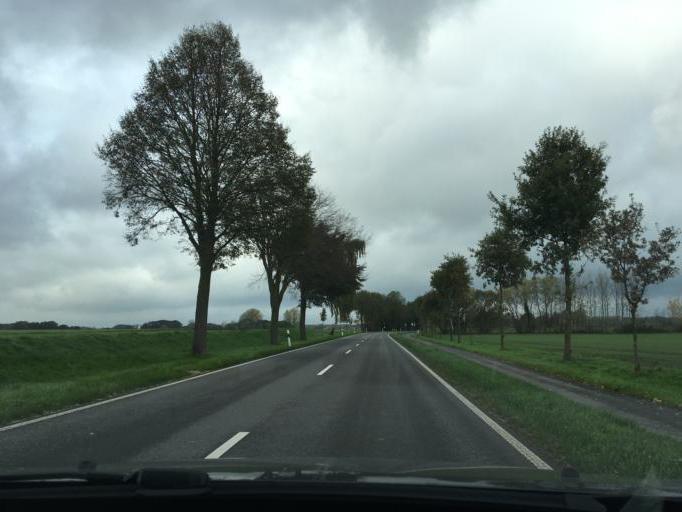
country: DE
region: North Rhine-Westphalia
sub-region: Regierungsbezirk Munster
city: Vreden
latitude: 52.0862
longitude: 6.7776
